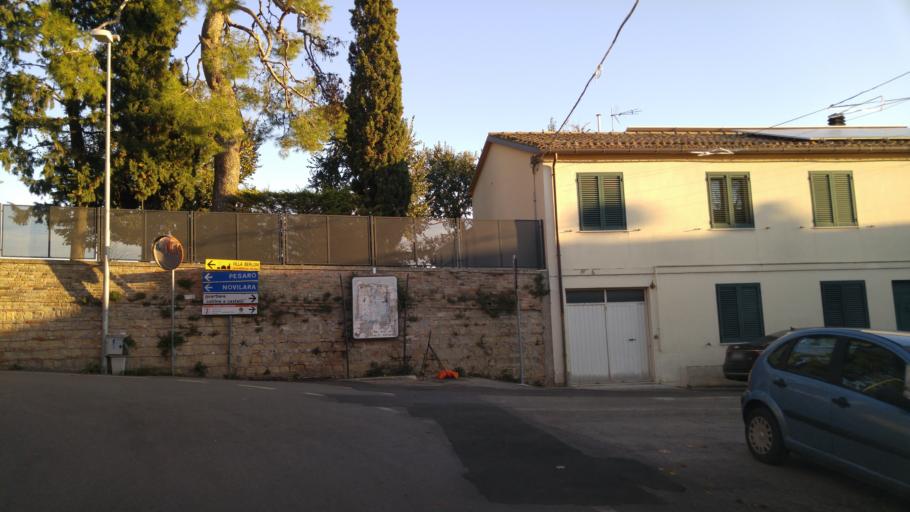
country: IT
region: The Marches
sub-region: Provincia di Pesaro e Urbino
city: Pesaro
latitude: 43.8568
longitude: 12.8873
